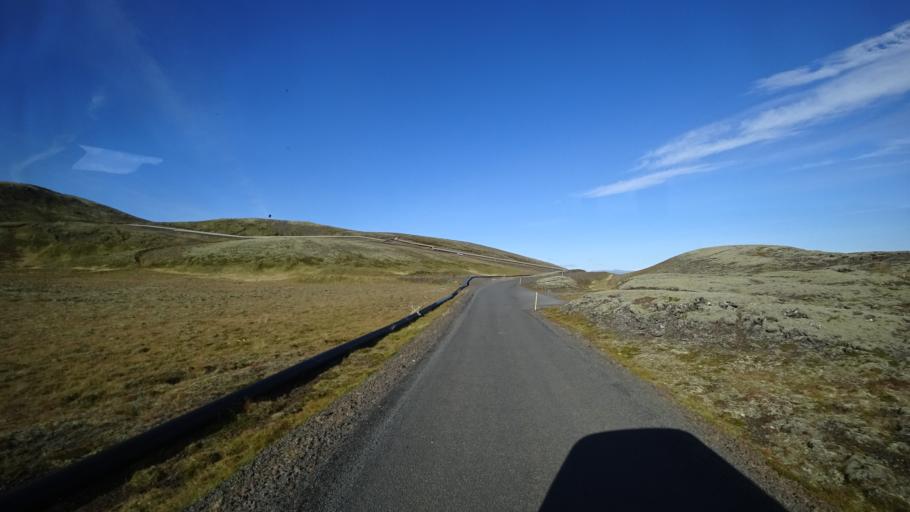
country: IS
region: South
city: Hveragerdi
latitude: 64.1053
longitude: -21.2766
